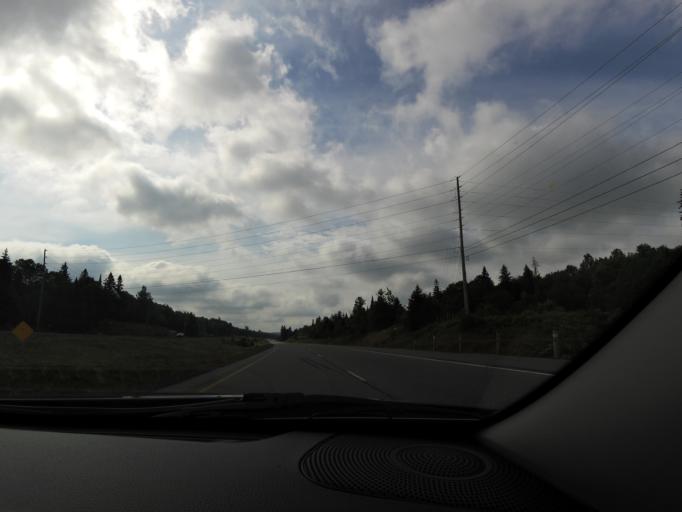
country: CA
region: Ontario
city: Huntsville
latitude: 45.3905
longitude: -79.2343
